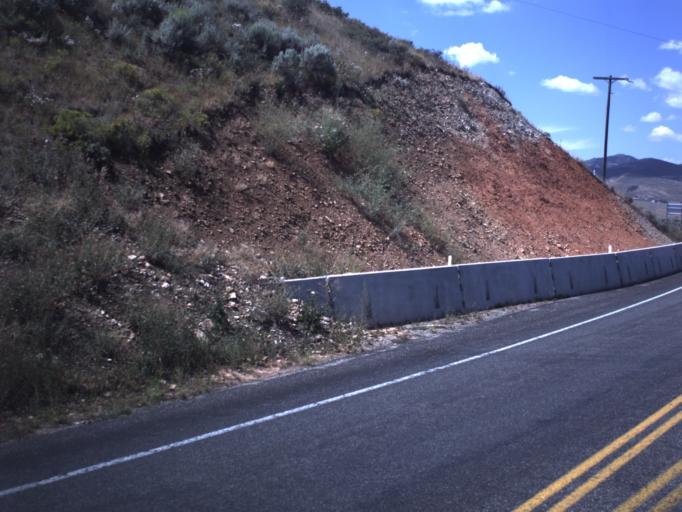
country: US
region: Utah
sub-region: Rich County
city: Randolph
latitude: 41.8986
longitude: -111.3682
